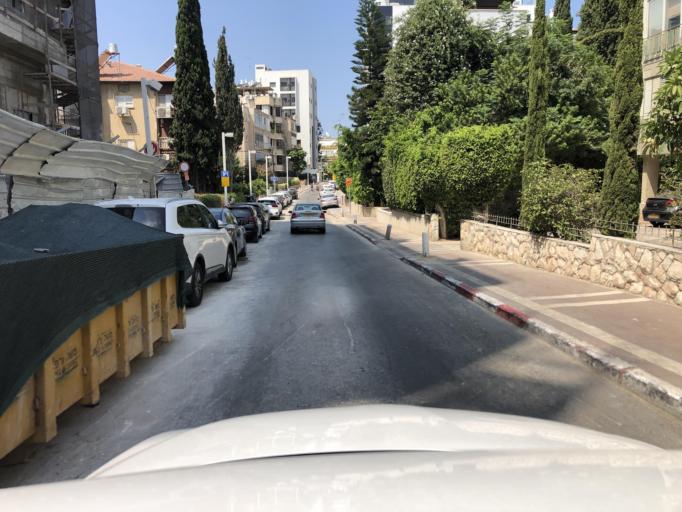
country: IL
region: Tel Aviv
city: Ramat Gan
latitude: 32.0768
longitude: 34.8061
